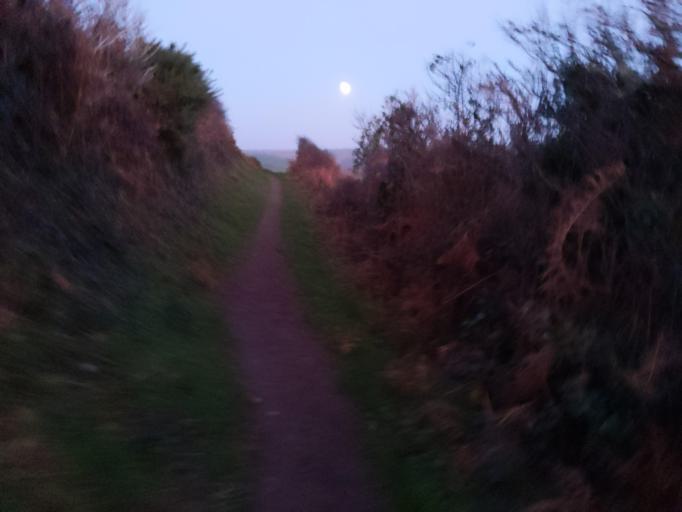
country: GB
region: England
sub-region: Cornwall
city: Fowey
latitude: 50.3289
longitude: -4.5938
